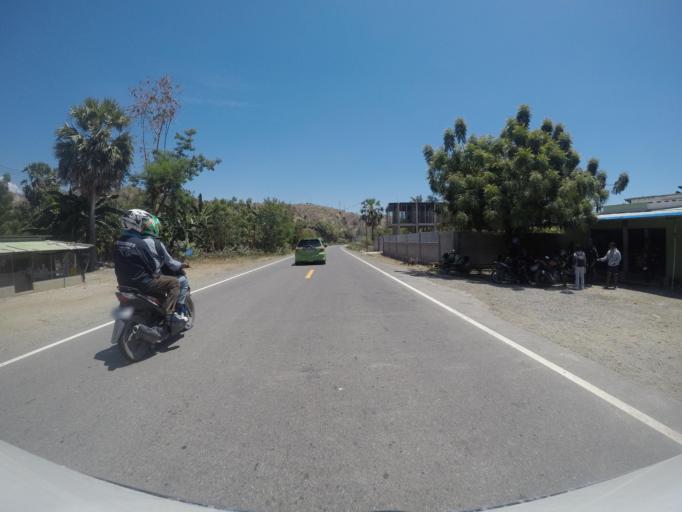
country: ID
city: Metinaro
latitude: -8.5372
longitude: 125.7055
